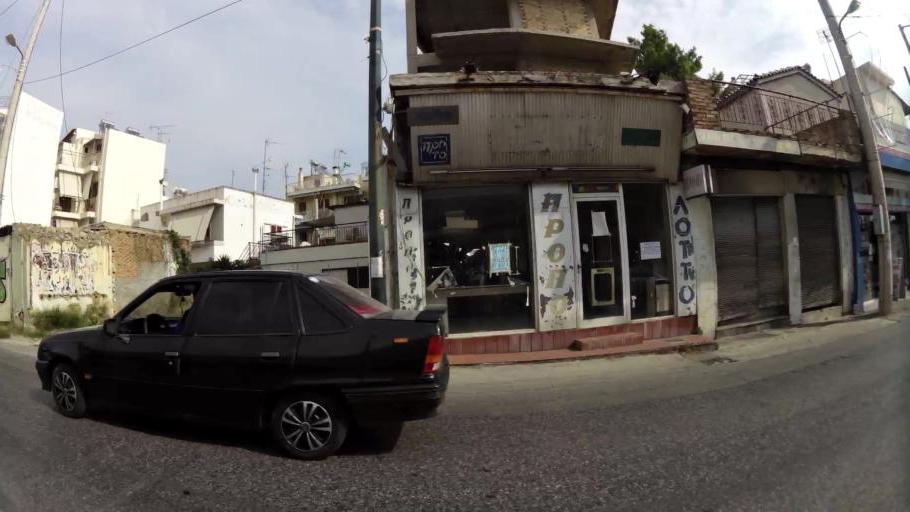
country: GR
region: Attica
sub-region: Nomarchia Athinas
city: Peristeri
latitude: 38.0213
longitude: 23.6856
